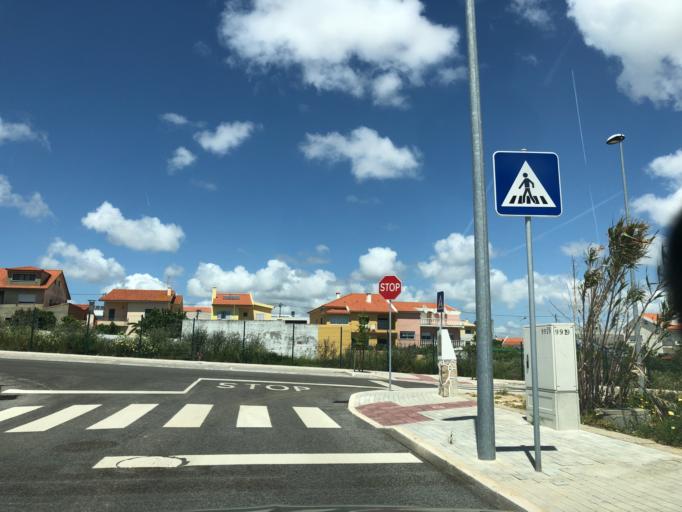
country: PT
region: Lisbon
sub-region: Cascais
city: Sao Domingos de Rana
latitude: 38.7052
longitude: -9.3279
